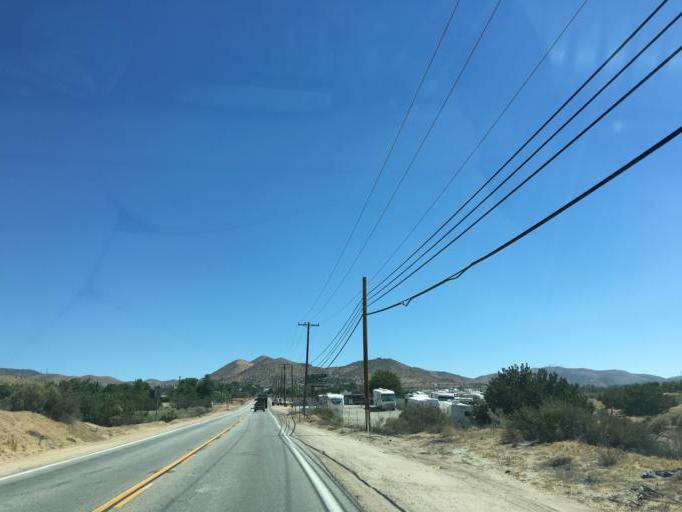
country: US
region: California
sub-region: Los Angeles County
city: Acton
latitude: 34.4761
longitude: -118.1707
